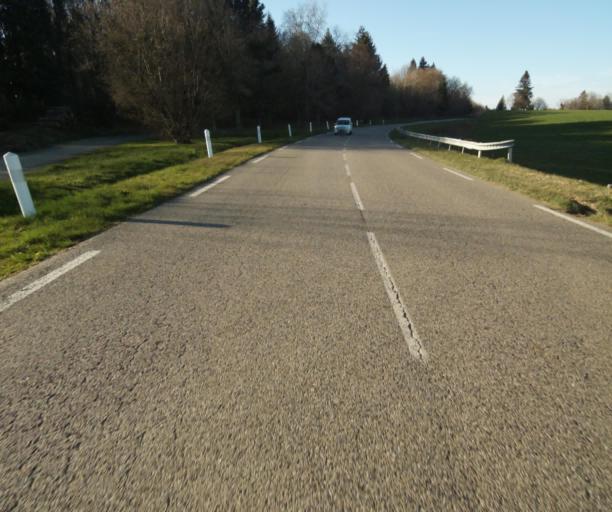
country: FR
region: Limousin
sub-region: Departement de la Correze
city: Seilhac
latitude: 45.3808
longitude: 1.7219
